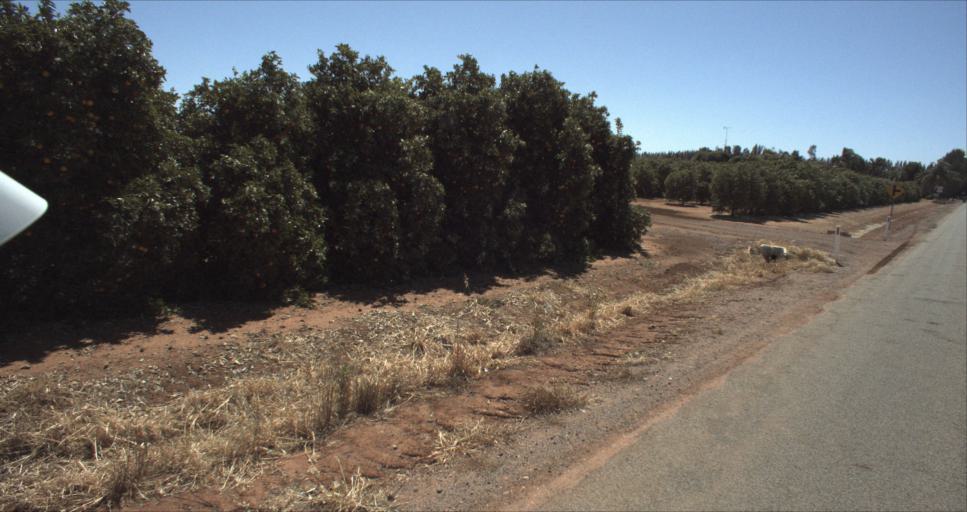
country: AU
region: New South Wales
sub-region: Leeton
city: Leeton
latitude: -34.5324
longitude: 146.3287
